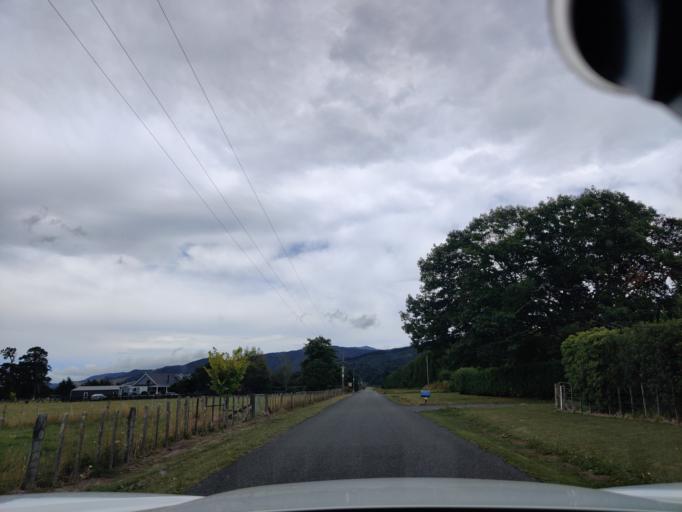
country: NZ
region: Wellington
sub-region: Masterton District
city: Masterton
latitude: -41.0366
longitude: 175.4379
